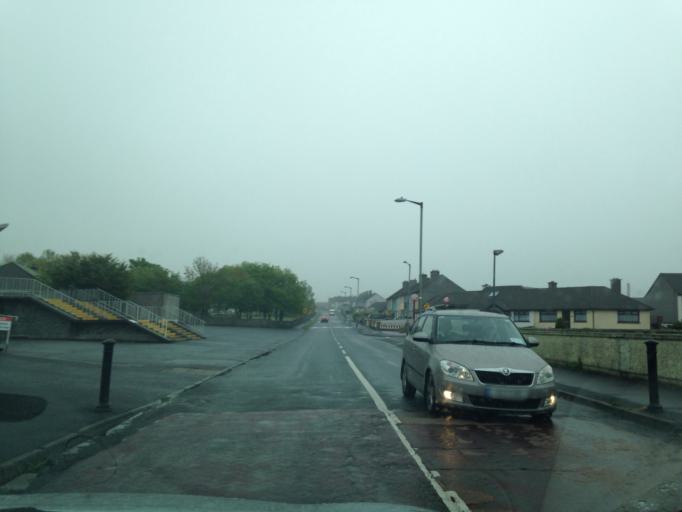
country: IE
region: Connaught
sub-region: County Galway
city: Gaillimh
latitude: 53.2815
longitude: -9.0166
